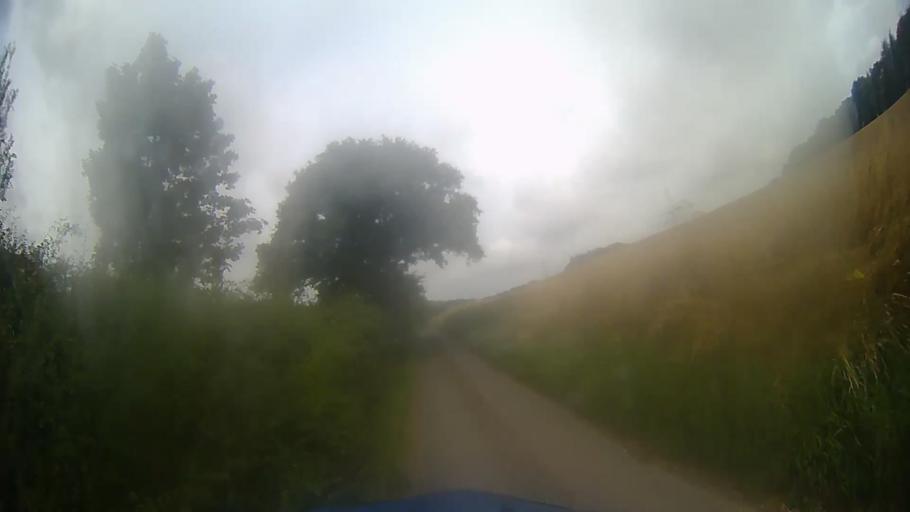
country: GB
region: England
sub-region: Hampshire
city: Overton
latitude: 51.2774
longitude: -1.3127
